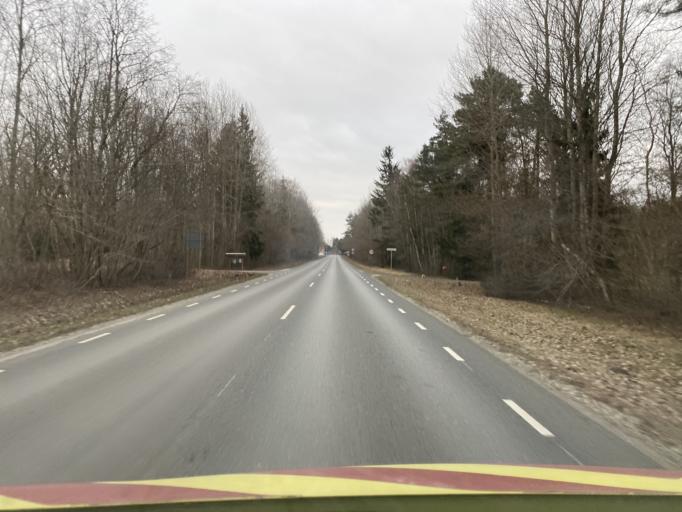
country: EE
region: Laeaene
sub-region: Ridala Parish
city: Uuemoisa
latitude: 58.9978
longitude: 23.7058
